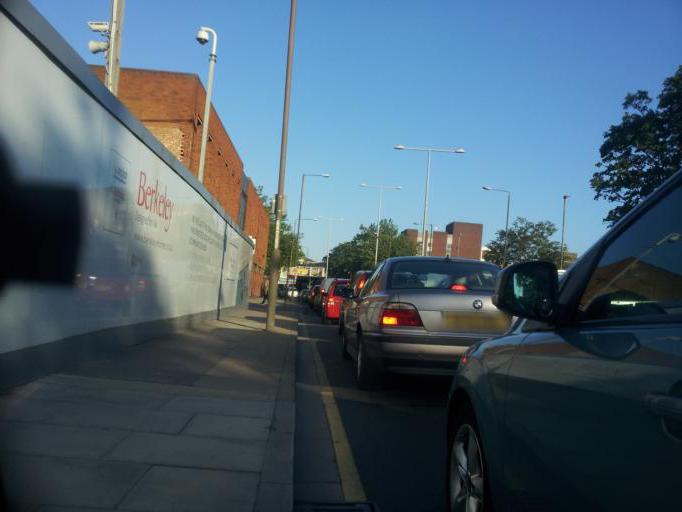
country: GB
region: England
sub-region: Greater London
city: Woolwich
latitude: 51.4924
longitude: 0.0674
